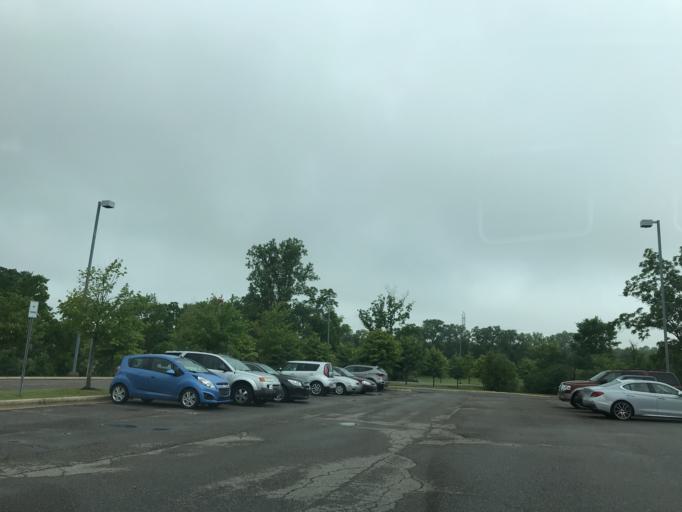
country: US
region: Michigan
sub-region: Washtenaw County
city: Ypsilanti
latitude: 42.2727
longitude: -83.6261
